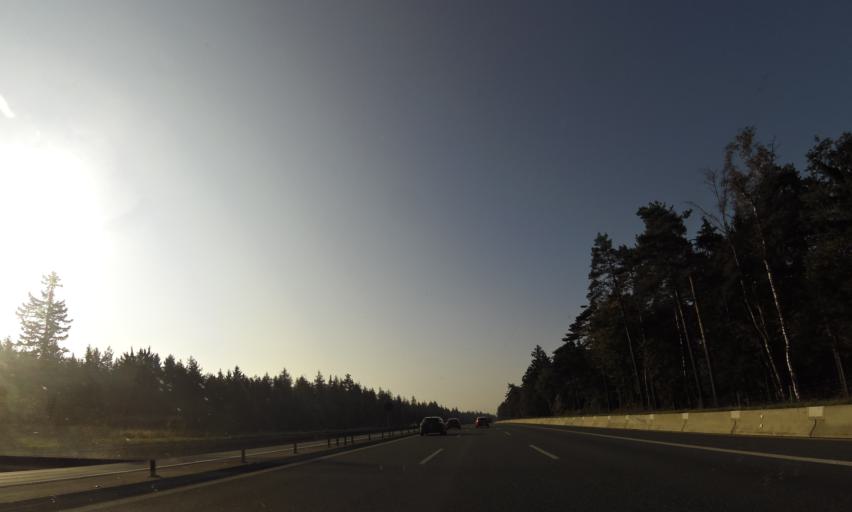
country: DE
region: Bavaria
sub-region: Upper Franconia
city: Gesees
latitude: 49.8625
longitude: 11.5181
